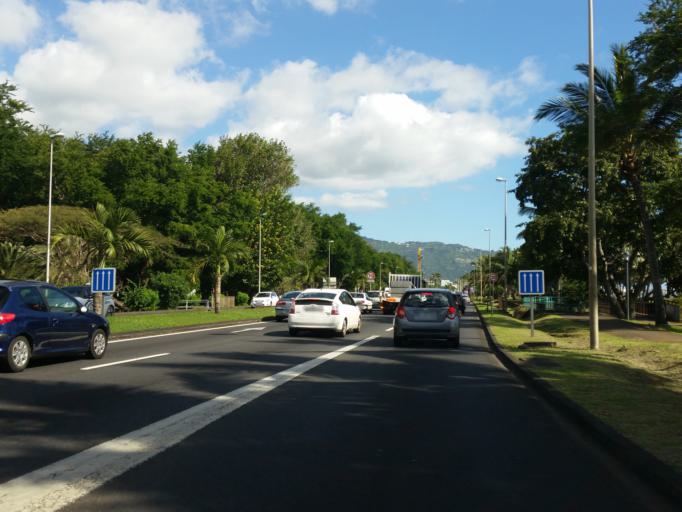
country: RE
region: Reunion
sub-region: Reunion
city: Saint-Denis
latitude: -20.8865
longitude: 55.4877
